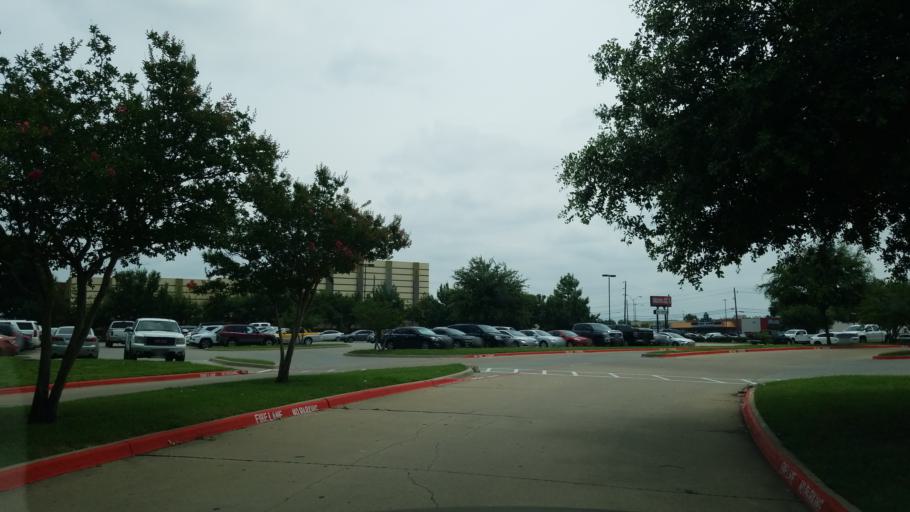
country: US
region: Texas
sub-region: Dallas County
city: Farmers Branch
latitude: 32.9106
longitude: -96.8767
